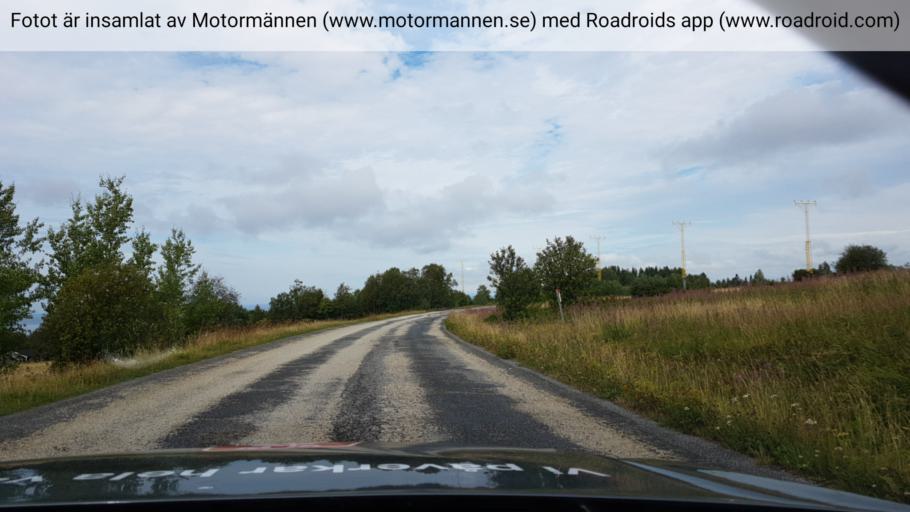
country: SE
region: Jaemtland
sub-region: Krokoms Kommun
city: Krokom
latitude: 63.1993
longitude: 14.4716
